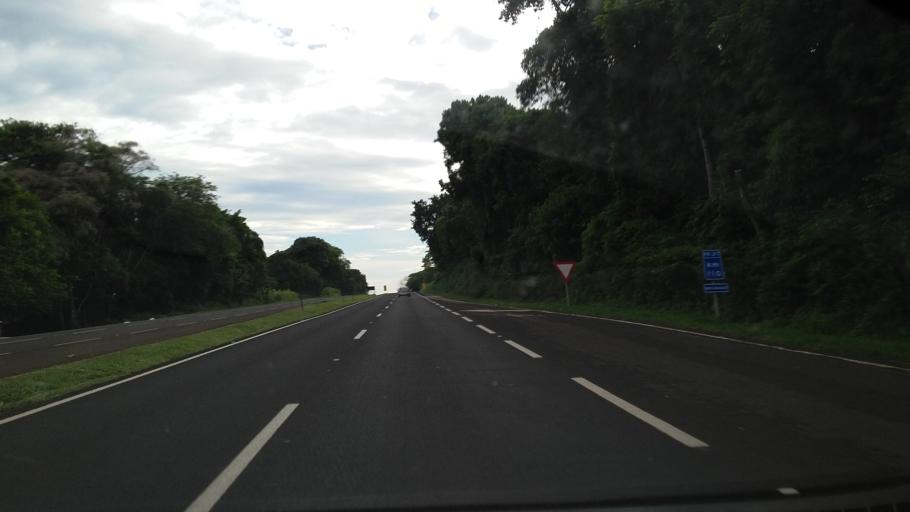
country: BR
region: Parana
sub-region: Paicandu
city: Paicandu
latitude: -23.5054
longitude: -52.0206
